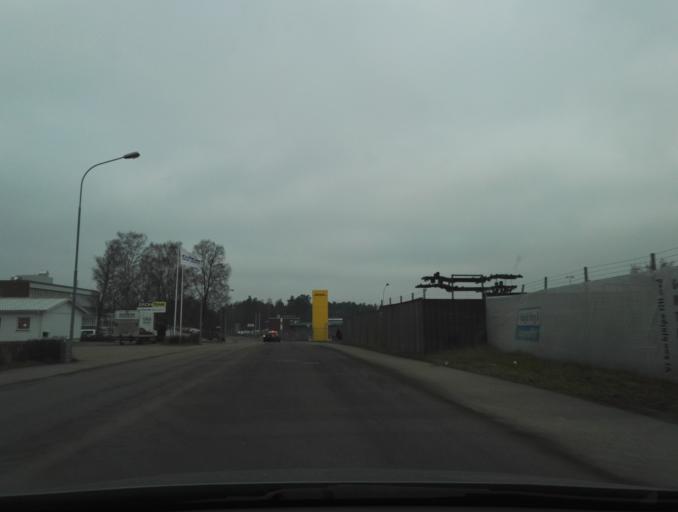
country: SE
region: Kronoberg
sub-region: Vaxjo Kommun
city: Vaexjoe
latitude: 56.8882
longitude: 14.7714
